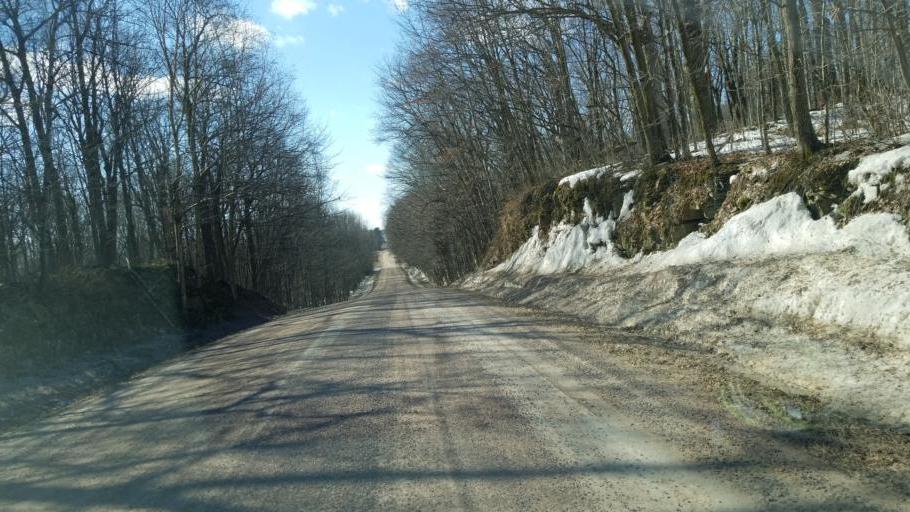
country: US
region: Wisconsin
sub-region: Clark County
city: Loyal
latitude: 44.6620
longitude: -90.4561
